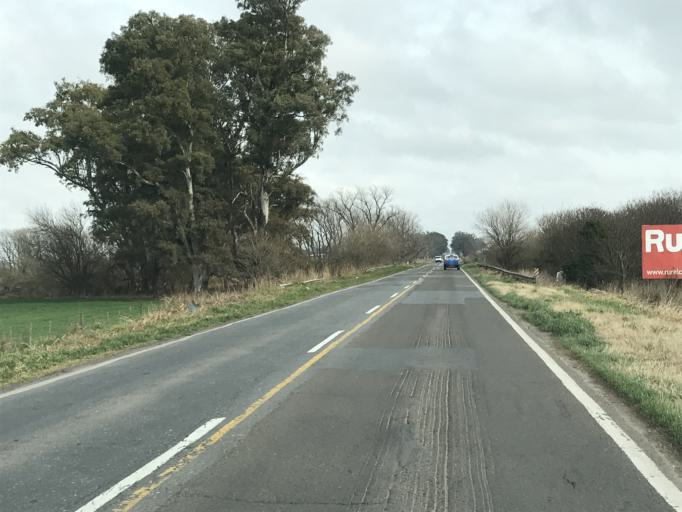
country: AR
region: Santa Fe
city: Canada de Gomez
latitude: -32.8249
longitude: -61.3098
